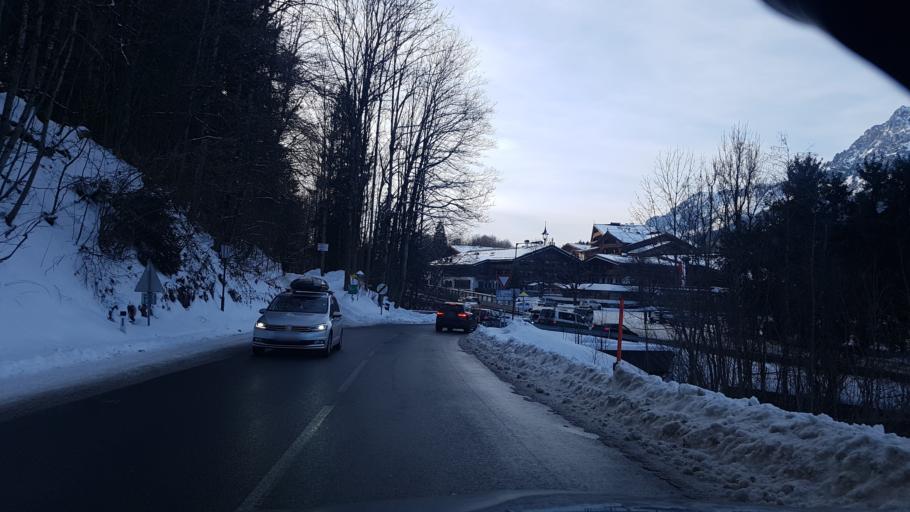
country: AT
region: Tyrol
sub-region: Politischer Bezirk Kitzbuhel
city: Oberndorf in Tirol
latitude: 47.5146
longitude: 12.3474
